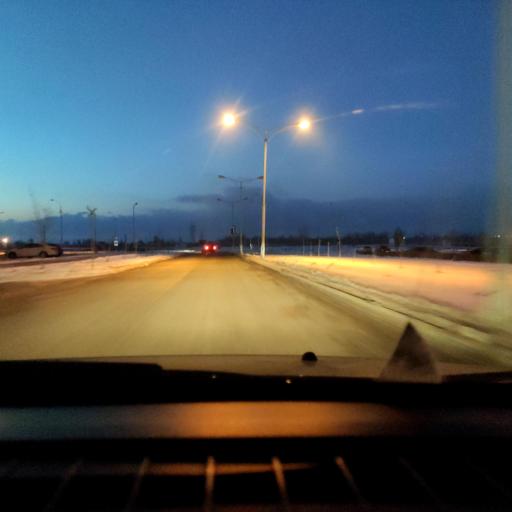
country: RU
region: Samara
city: Podstepki
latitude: 53.5563
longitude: 49.2142
